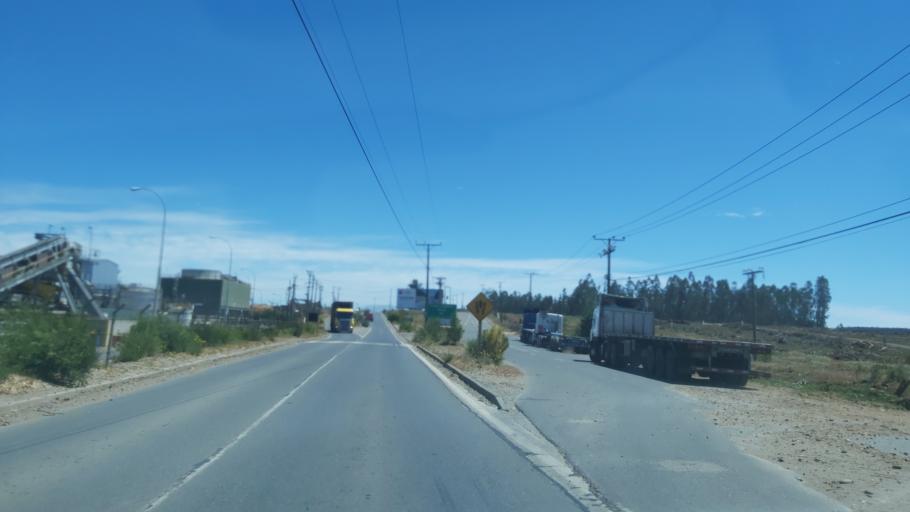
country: CL
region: Maule
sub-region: Provincia de Talca
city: Constitucion
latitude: -35.3689
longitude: -72.4104
